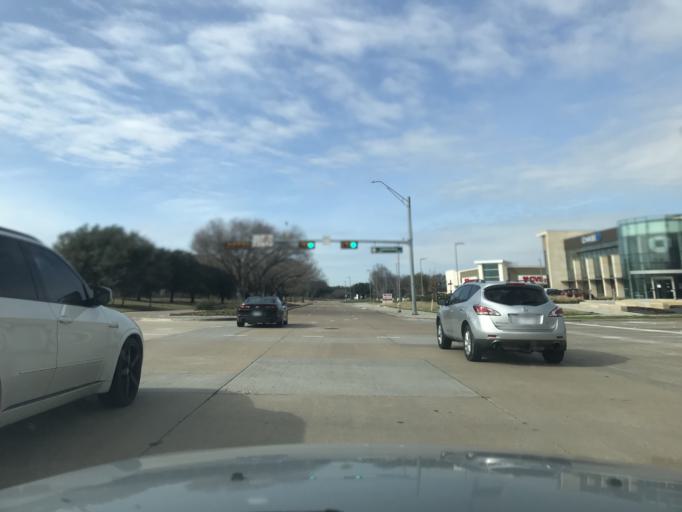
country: US
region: Texas
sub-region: Denton County
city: The Colony
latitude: 33.0781
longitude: -96.8281
